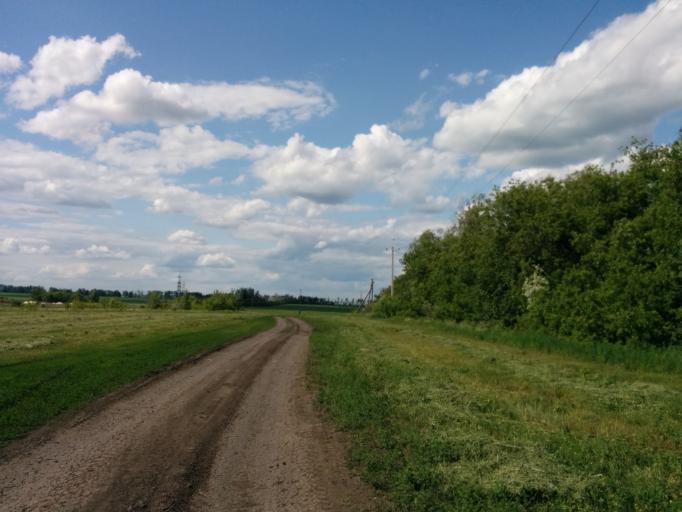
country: RU
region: Tambov
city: Tambov
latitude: 52.7920
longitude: 41.3833
